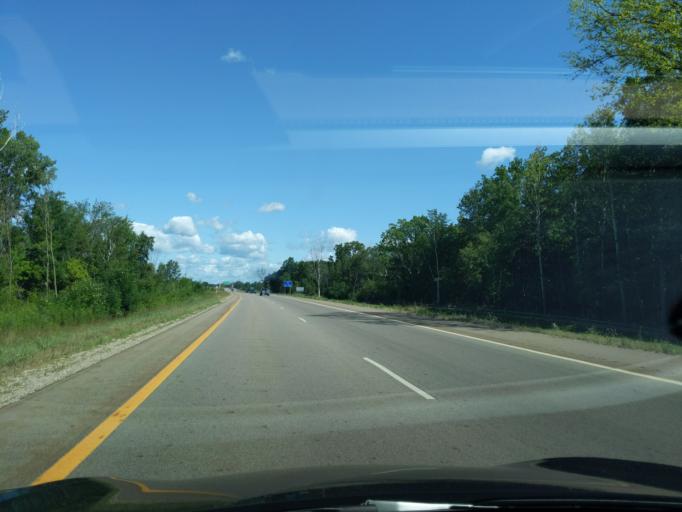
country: US
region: Michigan
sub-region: Gratiot County
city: Saint Louis
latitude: 43.3693
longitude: -84.6004
